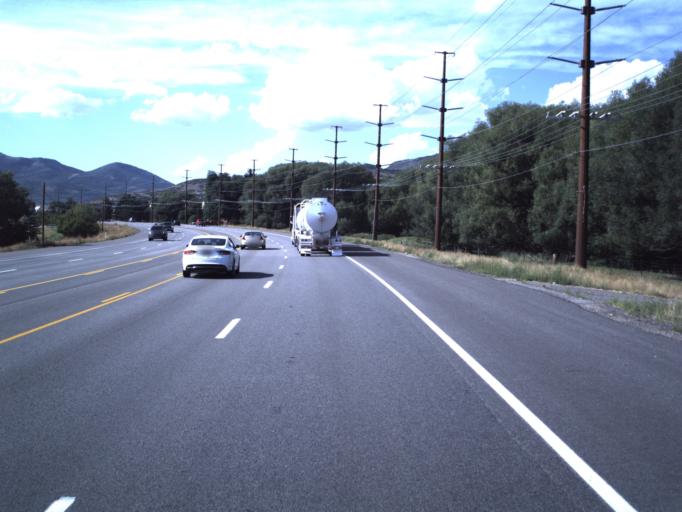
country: US
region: Utah
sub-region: Wasatch County
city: Heber
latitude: 40.5331
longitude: -111.4093
